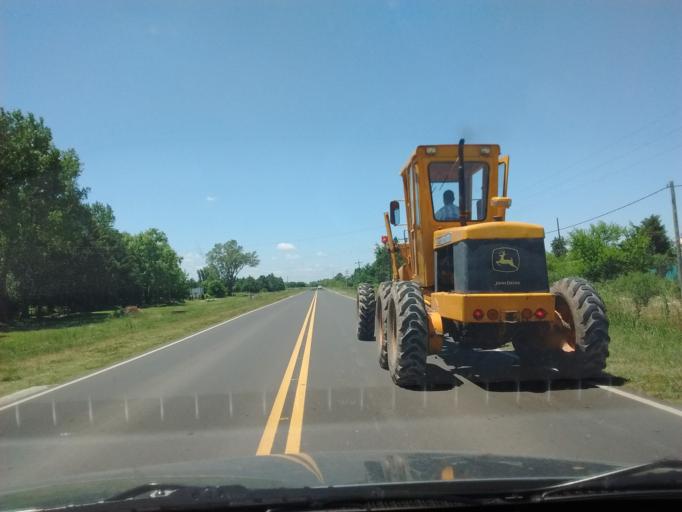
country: AR
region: Entre Rios
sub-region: Departamento de Gualeguay
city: Gualeguay
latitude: -33.1165
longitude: -59.3538
